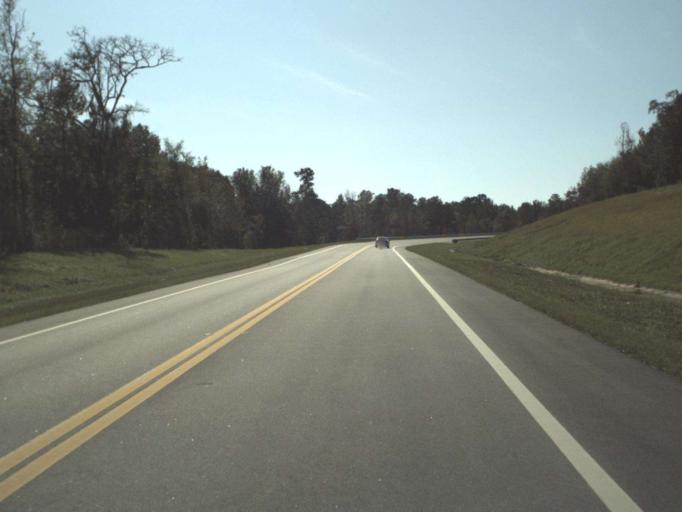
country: US
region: Florida
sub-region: Gadsden County
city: Quincy
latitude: 30.5762
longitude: -84.5481
